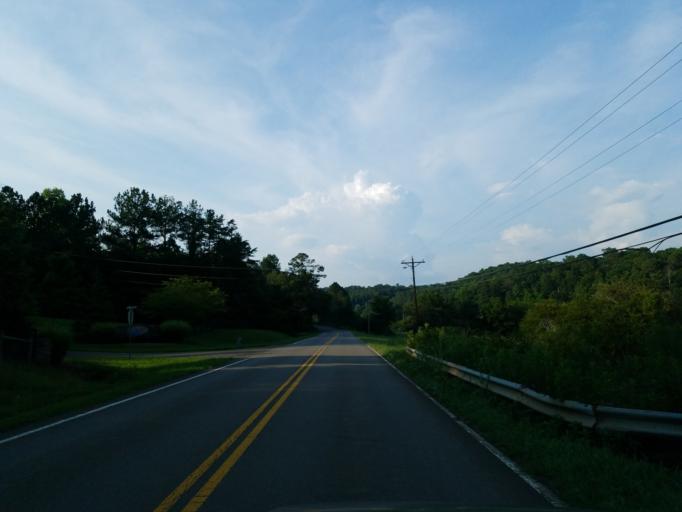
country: US
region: Georgia
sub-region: Gilmer County
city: Ellijay
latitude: 34.5686
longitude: -84.5361
